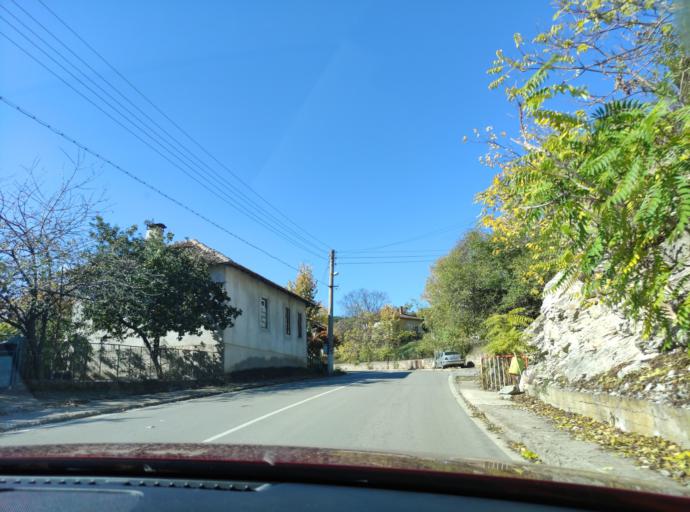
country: BG
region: Montana
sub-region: Obshtina Chiprovtsi
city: Chiprovtsi
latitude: 43.4338
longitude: 22.9732
